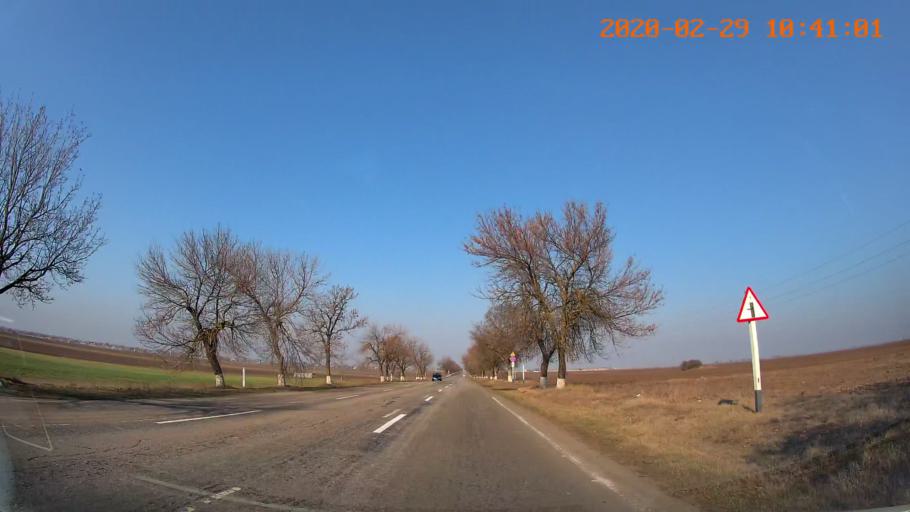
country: MD
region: Telenesti
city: Grigoriopol
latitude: 47.0385
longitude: 29.4312
